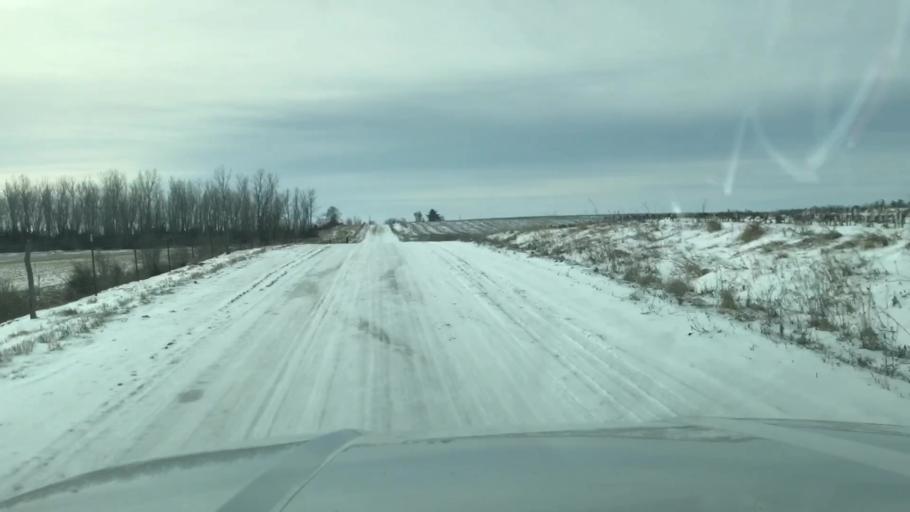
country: US
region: Missouri
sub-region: Holt County
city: Mound City
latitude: 40.1366
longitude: -95.0696
